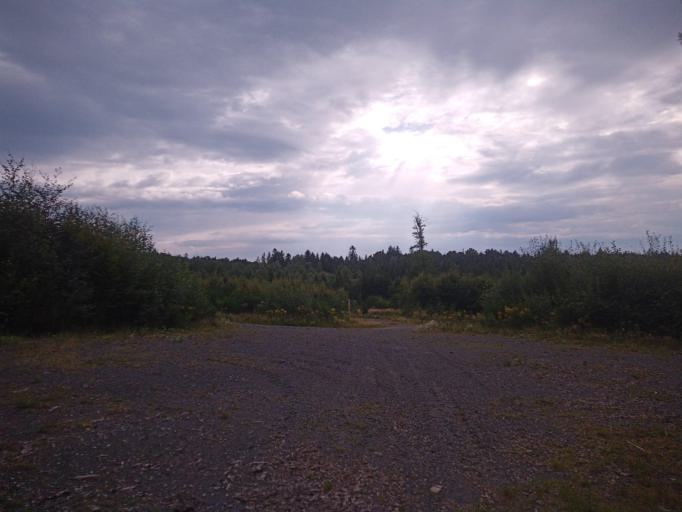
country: PL
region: Lower Silesian Voivodeship
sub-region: Powiat lubanski
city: Lesna
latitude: 50.9955
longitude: 15.3064
